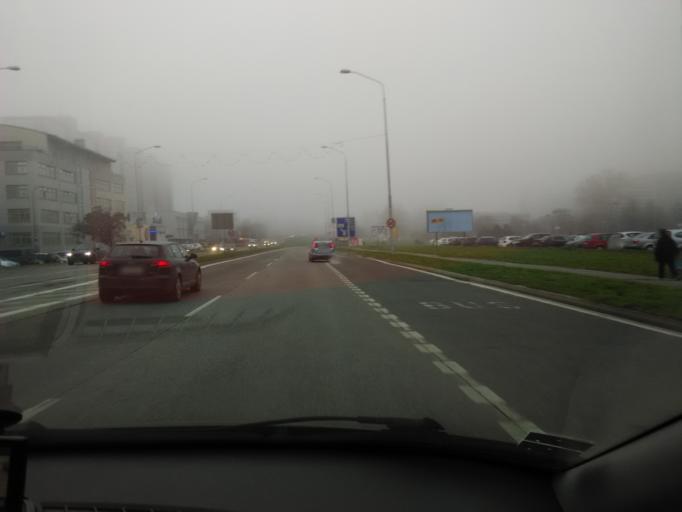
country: SK
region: Bratislavsky
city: Bratislava
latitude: 48.1245
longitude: 17.1322
